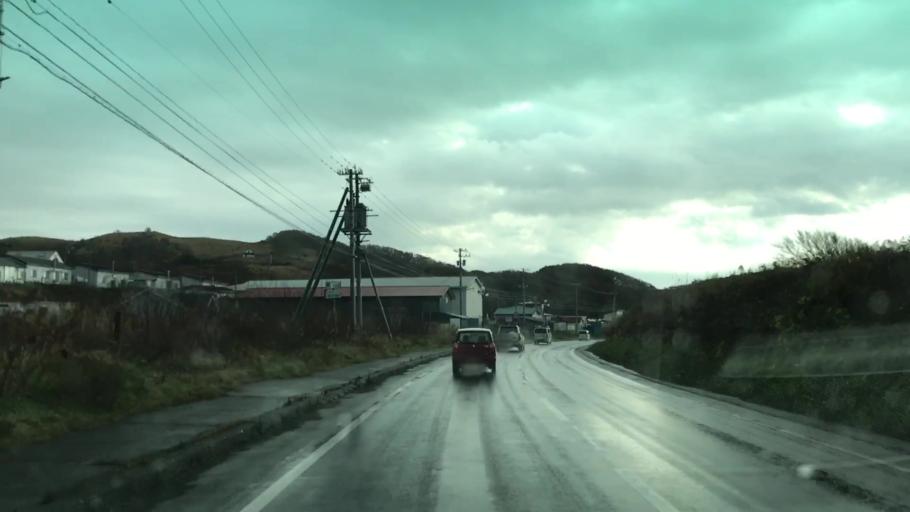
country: JP
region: Hokkaido
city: Shizunai-furukawacho
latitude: 42.1910
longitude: 142.6952
